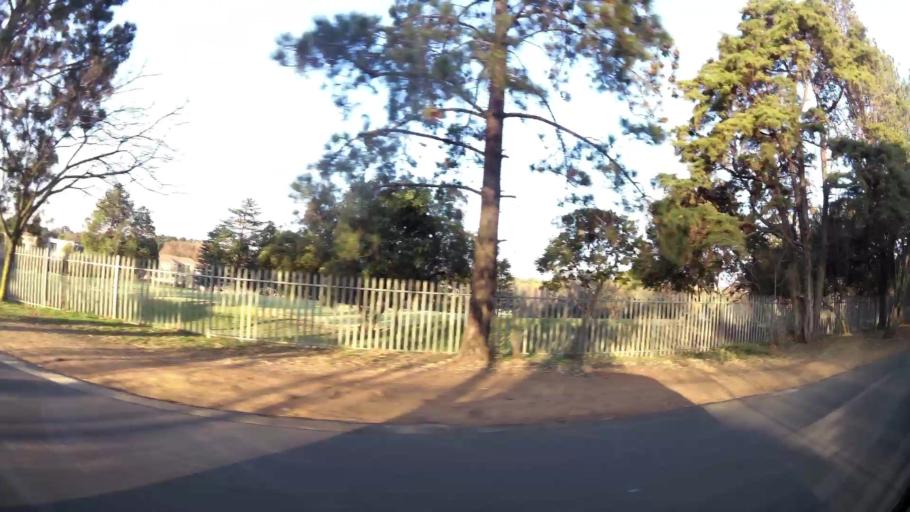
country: ZA
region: Gauteng
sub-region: City of Johannesburg Metropolitan Municipality
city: Johannesburg
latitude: -26.1570
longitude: 28.0557
